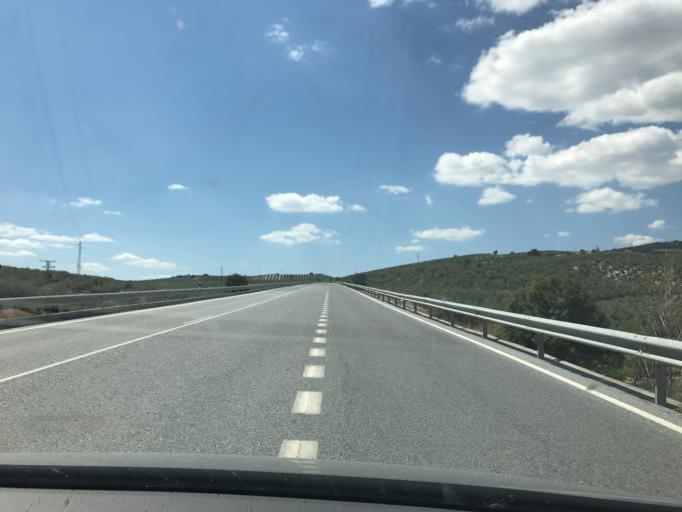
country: ES
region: Andalusia
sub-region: Provincia de Granada
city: Benalua de las Villas
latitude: 37.4278
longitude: -3.7363
